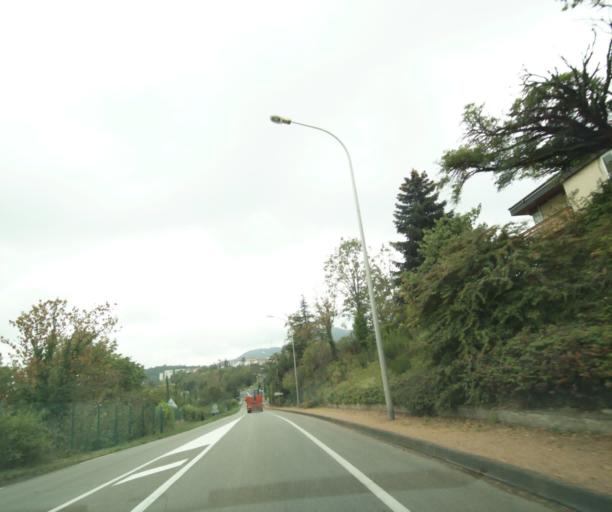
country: FR
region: Auvergne
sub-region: Departement du Puy-de-Dome
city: Royat
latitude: 45.7526
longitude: 3.0623
